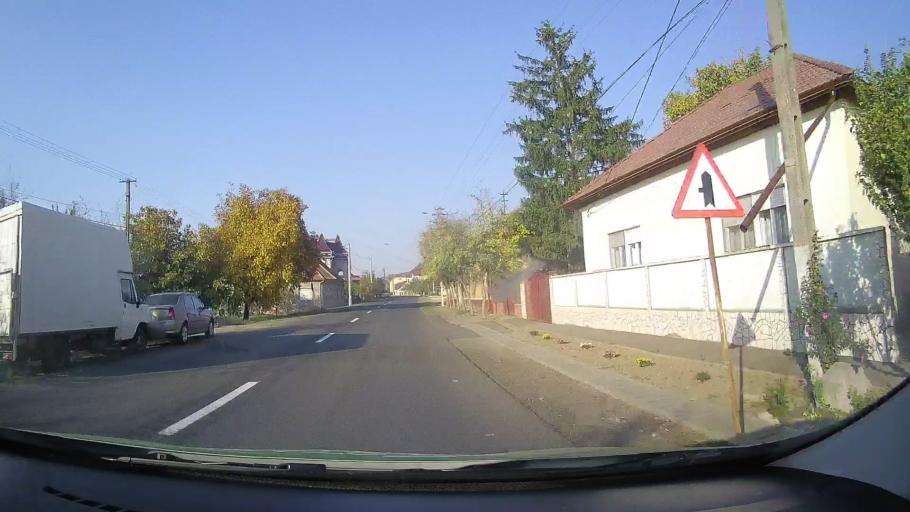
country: RO
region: Arad
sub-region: Comuna Covasint
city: Covasint
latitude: 46.1993
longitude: 21.6084
